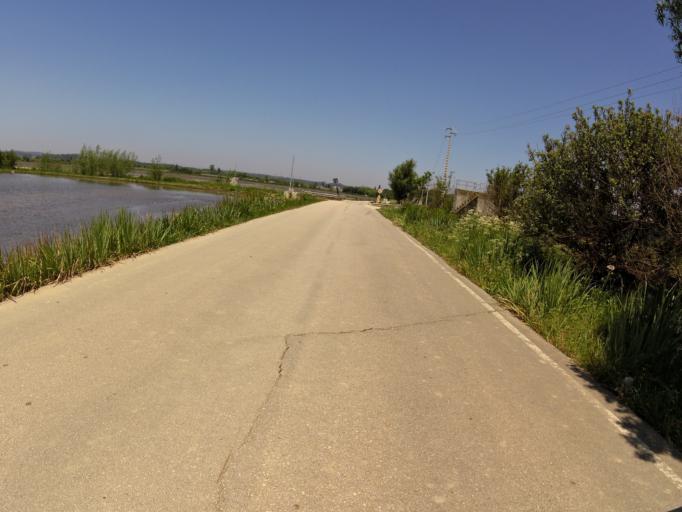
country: PT
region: Coimbra
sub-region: Montemor-O-Velho
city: Montemor-o-Velho
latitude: 40.1645
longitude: -8.7176
